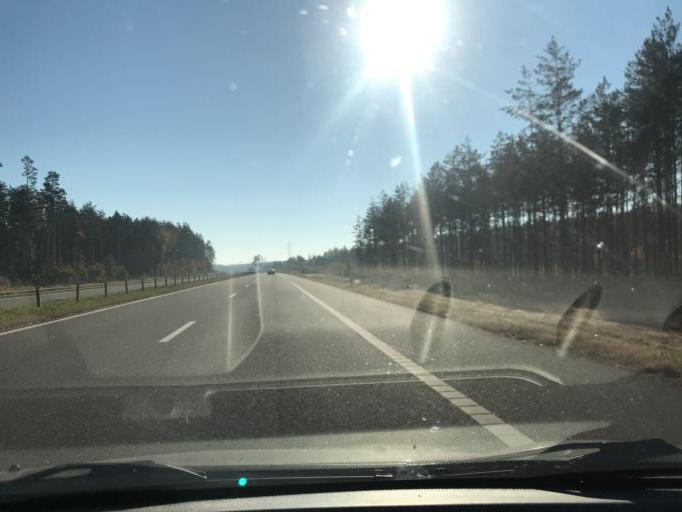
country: BY
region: Mogilev
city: Asipovichy
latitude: 53.4189
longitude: 28.4626
